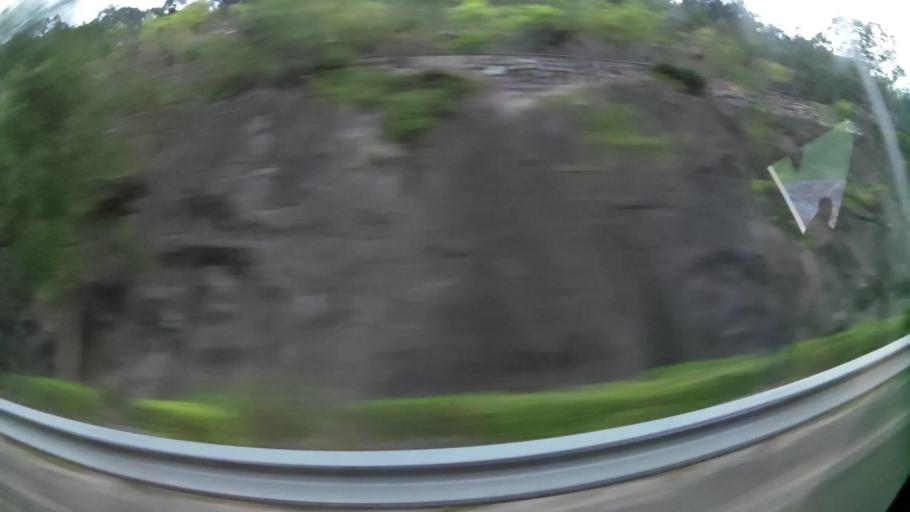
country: HK
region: Tsuen Wan
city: Tsuen Wan
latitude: 22.3555
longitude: 114.0853
